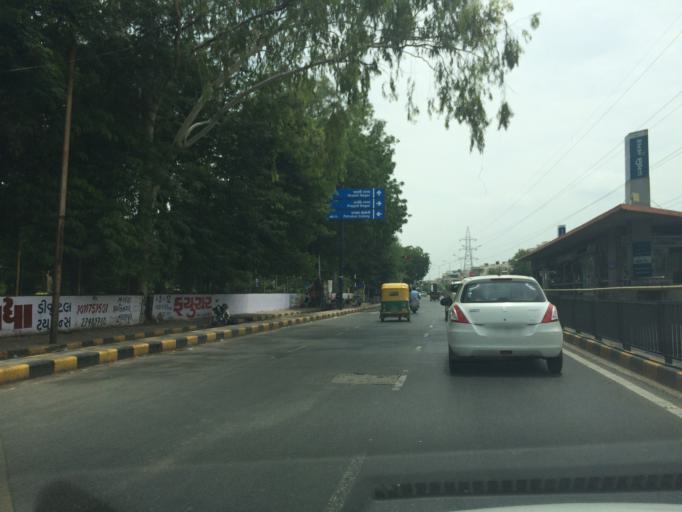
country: IN
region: Gujarat
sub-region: Ahmadabad
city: Ahmedabad
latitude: 23.0648
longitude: 72.5565
